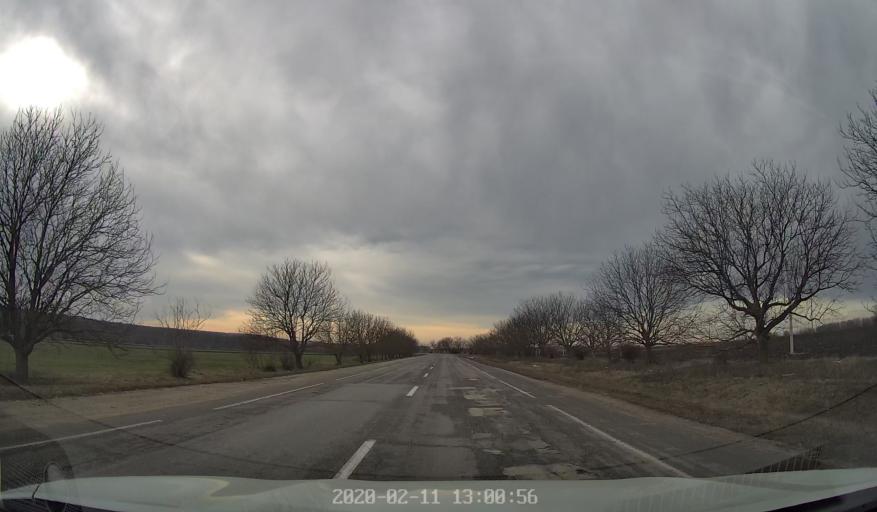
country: MD
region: Briceni
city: Briceni
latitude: 48.3228
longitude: 27.0112
